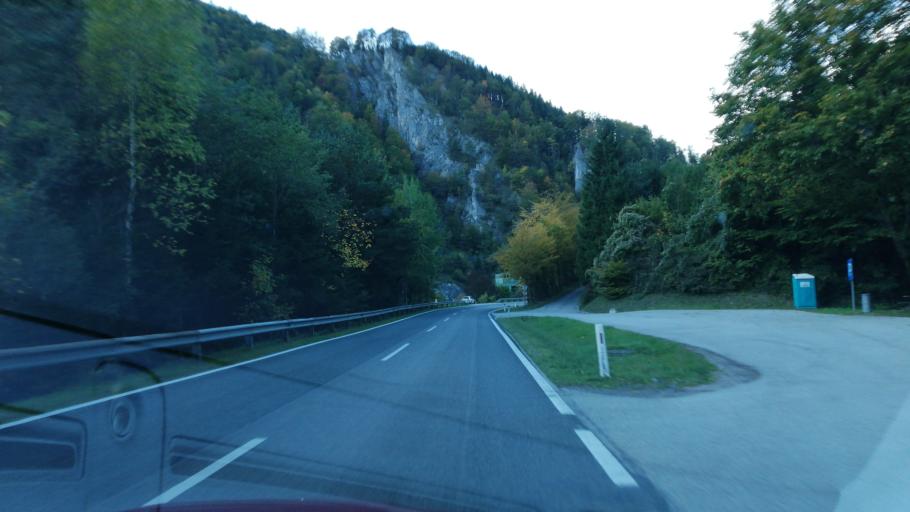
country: AT
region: Styria
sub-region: Politischer Bezirk Liezen
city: Altenmarkt bei Sankt Gallen
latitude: 47.7733
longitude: 14.6516
